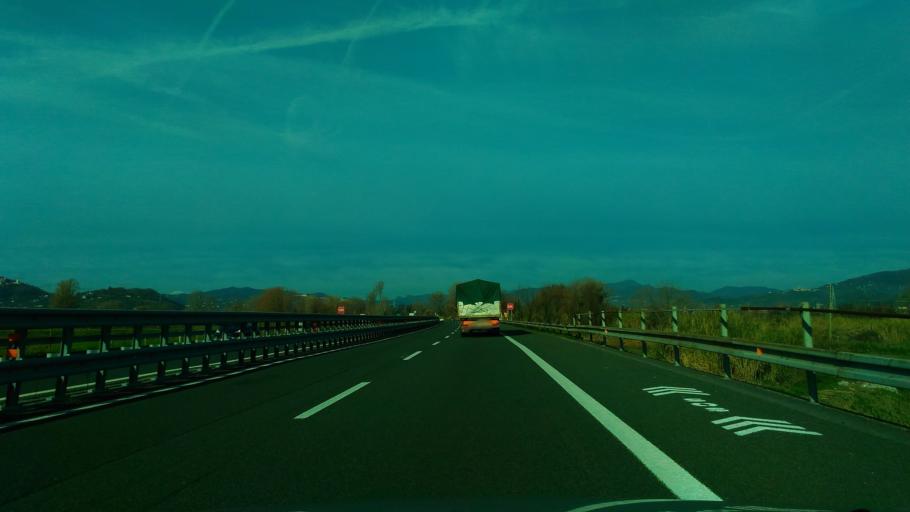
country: IT
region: Liguria
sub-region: Provincia di La Spezia
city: Sarzana
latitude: 44.0911
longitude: 9.9696
